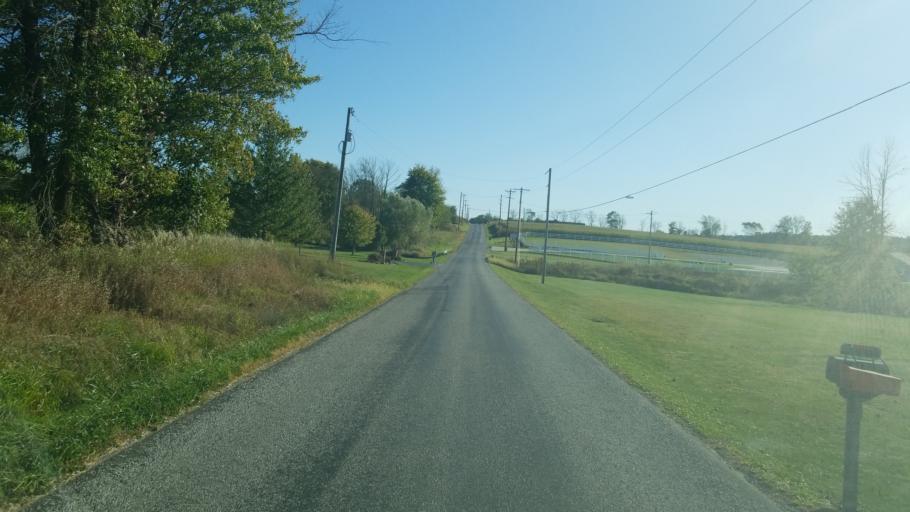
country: US
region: Ohio
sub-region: Wayne County
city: Creston
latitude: 40.9384
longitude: -81.9757
